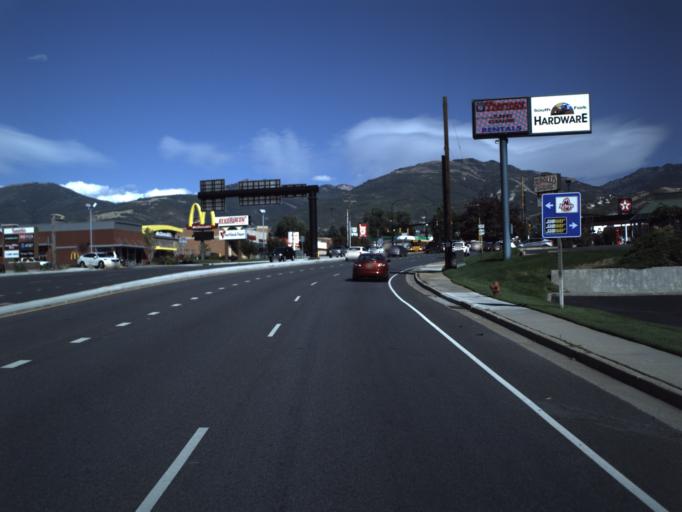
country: US
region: Utah
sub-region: Davis County
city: Woods Cross
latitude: 40.8614
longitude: -111.8989
